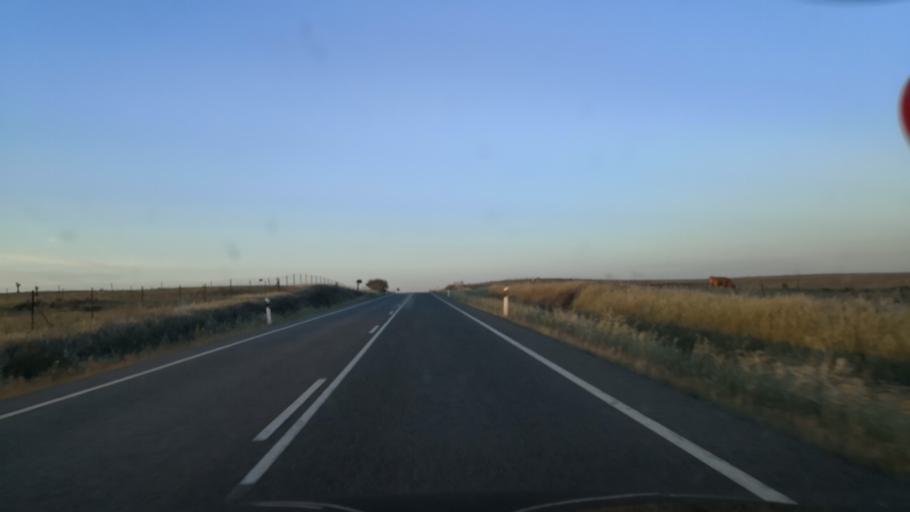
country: ES
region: Extremadura
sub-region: Provincia de Caceres
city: Alcantara
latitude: 39.6659
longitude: -6.8781
